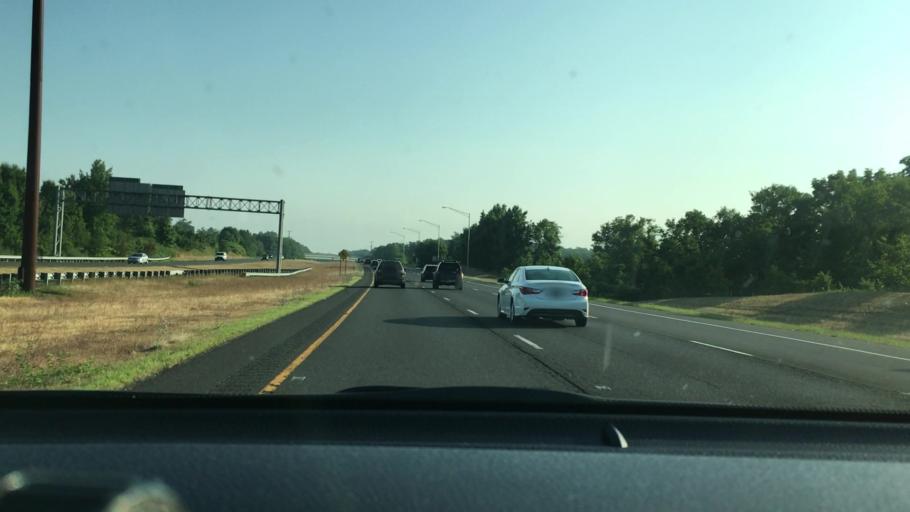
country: US
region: New Jersey
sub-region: Gloucester County
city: Richwood
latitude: 39.7221
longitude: -75.1532
